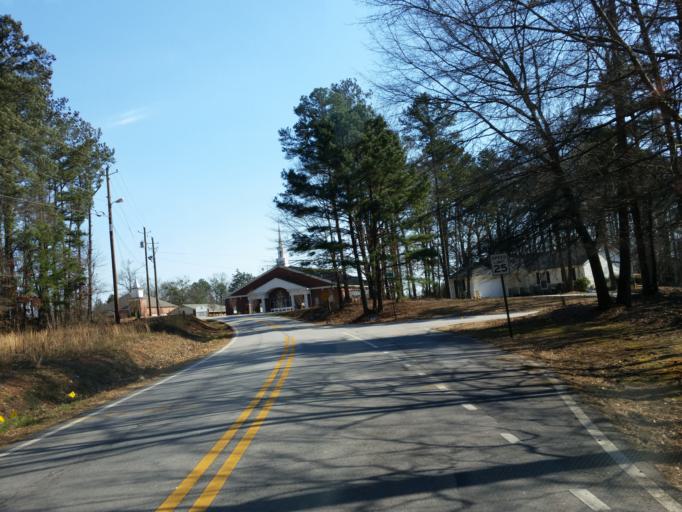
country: US
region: Georgia
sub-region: Henry County
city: Stockbridge
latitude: 33.4744
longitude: -84.2239
